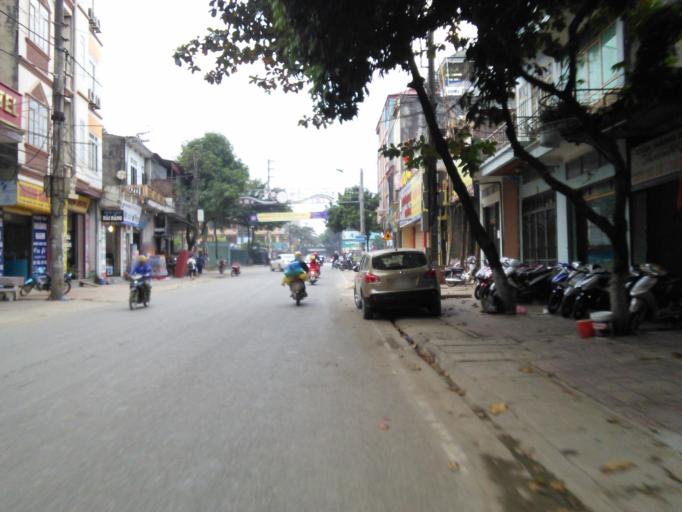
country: VN
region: Lao Cai
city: Lao Cai
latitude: 22.4907
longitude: 103.9782
